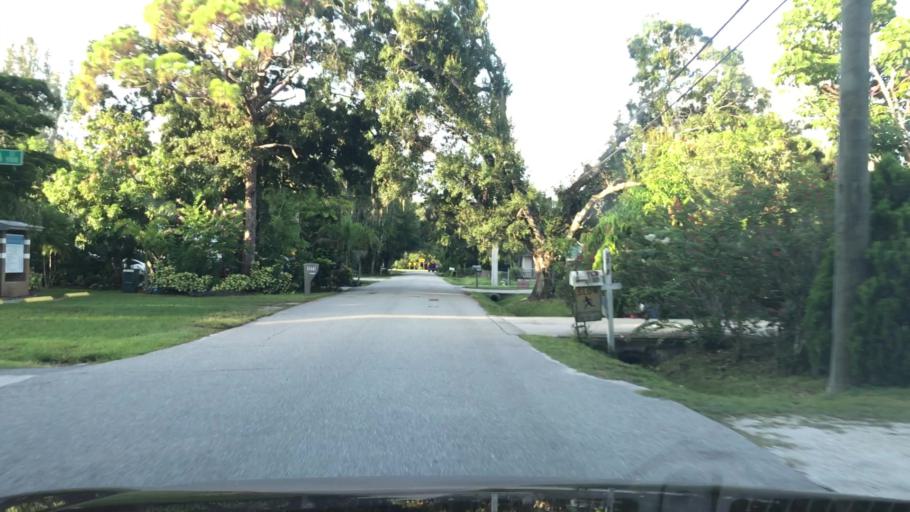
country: US
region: Florida
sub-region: Sarasota County
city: Fruitville
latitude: 27.3249
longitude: -82.4593
